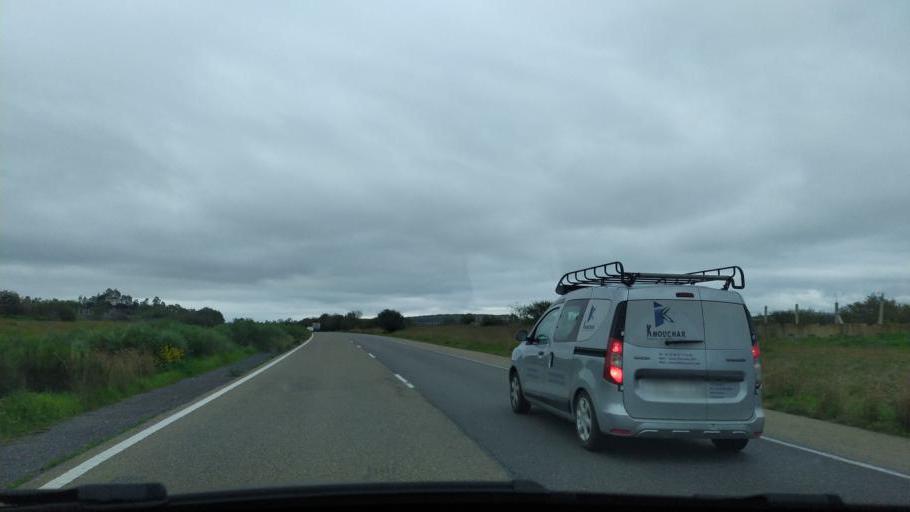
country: MA
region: Gharb-Chrarda-Beni Hssen
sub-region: Kenitra Province
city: Lalla Mimouna
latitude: 34.7941
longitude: -6.2978
